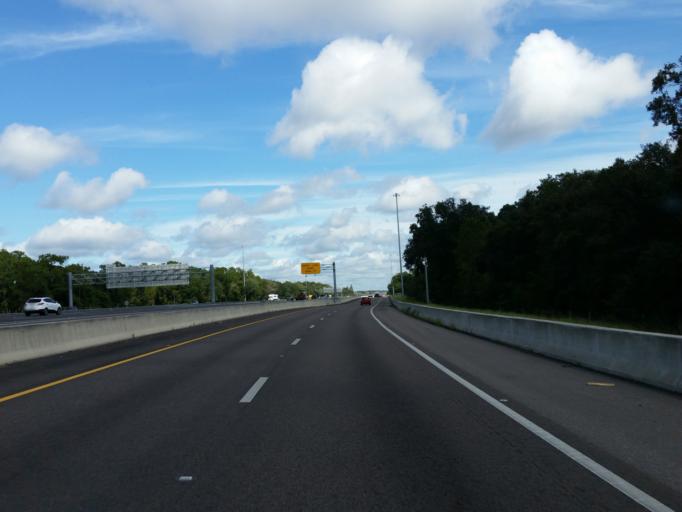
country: US
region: Florida
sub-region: Hillsborough County
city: Pebble Creek
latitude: 28.1748
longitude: -82.3918
